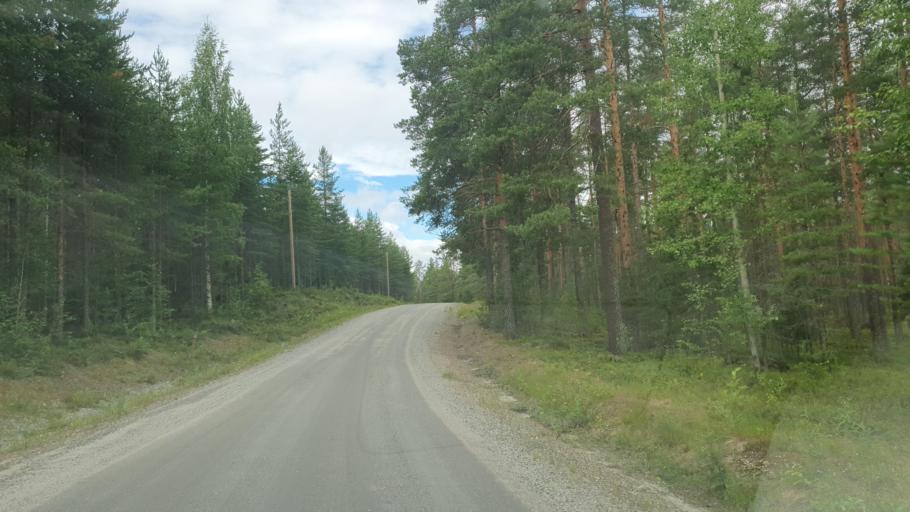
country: FI
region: Kainuu
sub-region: Kehys-Kainuu
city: Kuhmo
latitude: 64.1031
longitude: 29.4007
